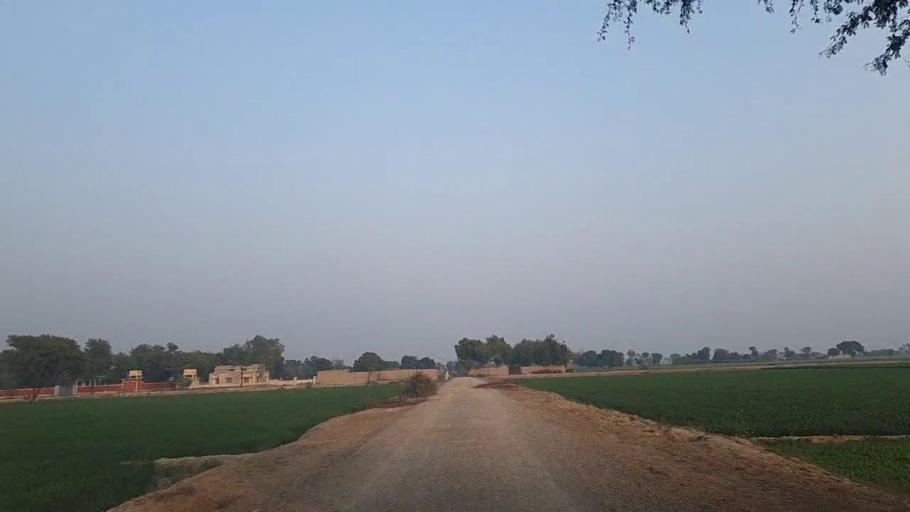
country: PK
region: Sindh
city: Nawabshah
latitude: 26.2694
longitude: 68.4554
